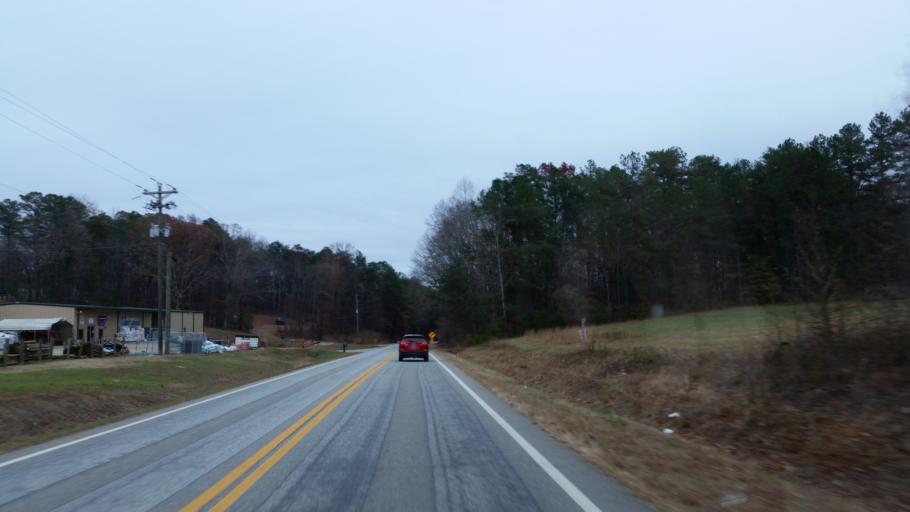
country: US
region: Georgia
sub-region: Dawson County
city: Dawsonville
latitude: 34.4395
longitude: -84.0835
